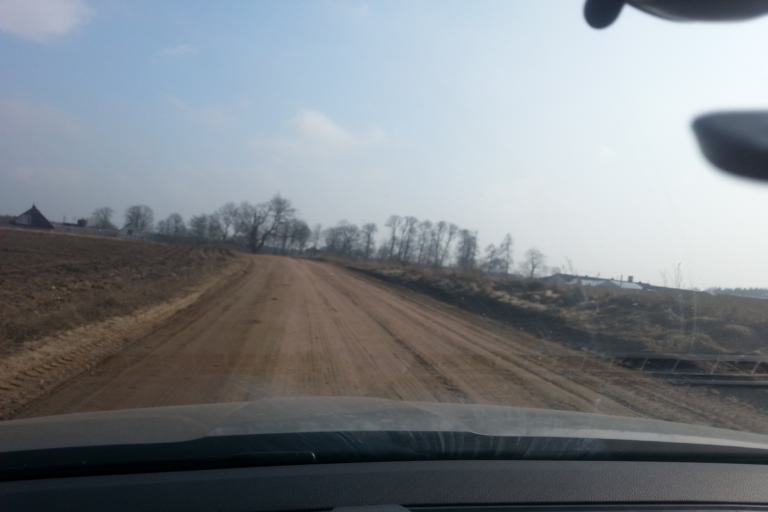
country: LT
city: Trakai
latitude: 54.4992
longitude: 24.9757
